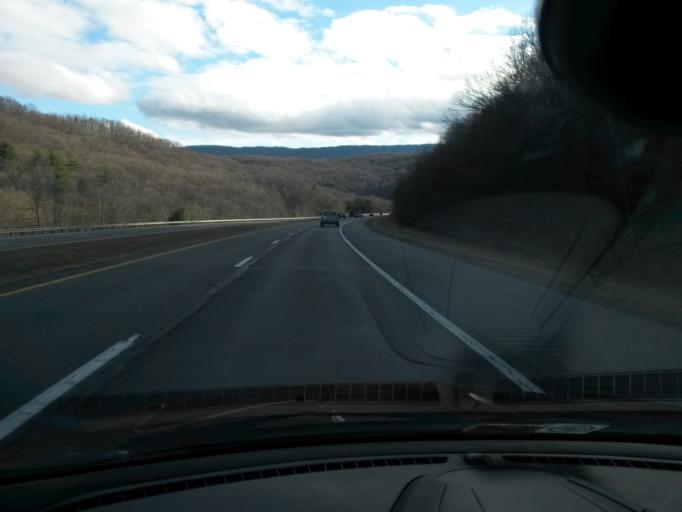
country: US
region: West Virginia
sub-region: Mercer County
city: Athens
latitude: 37.3488
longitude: -81.0139
